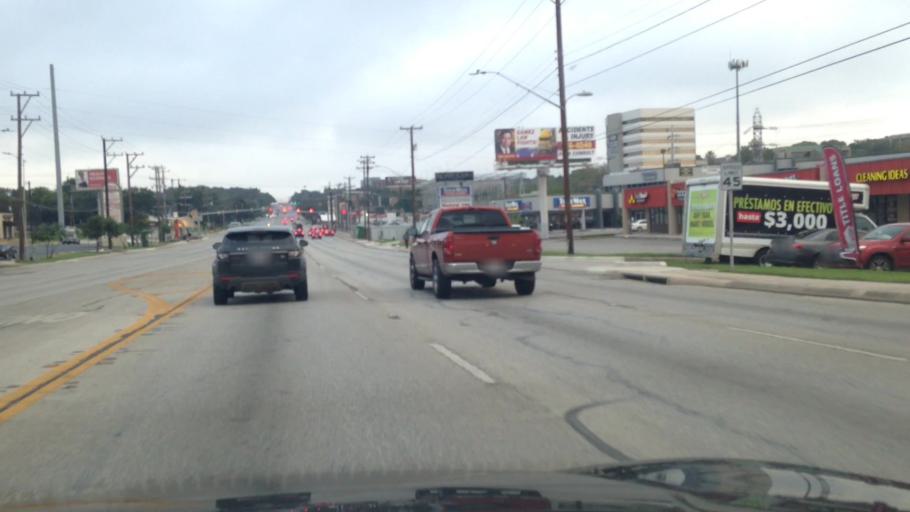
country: US
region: Texas
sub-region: Bexar County
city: Balcones Heights
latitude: 29.5012
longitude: -98.5589
